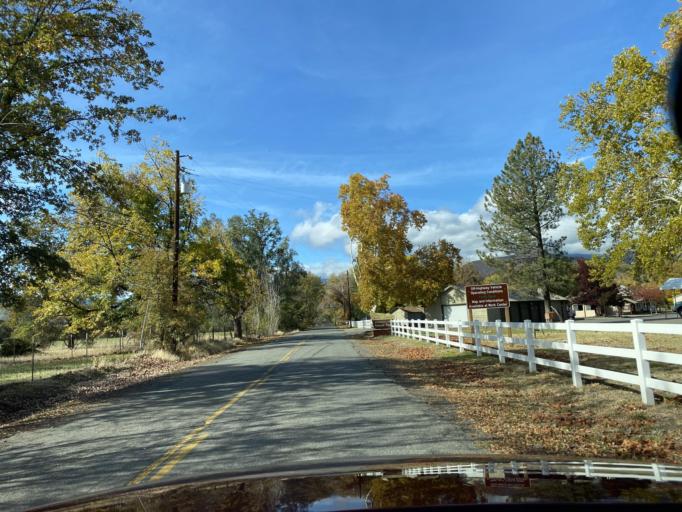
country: US
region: California
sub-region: Colusa County
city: Maxwell
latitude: 39.3779
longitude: -122.5484
